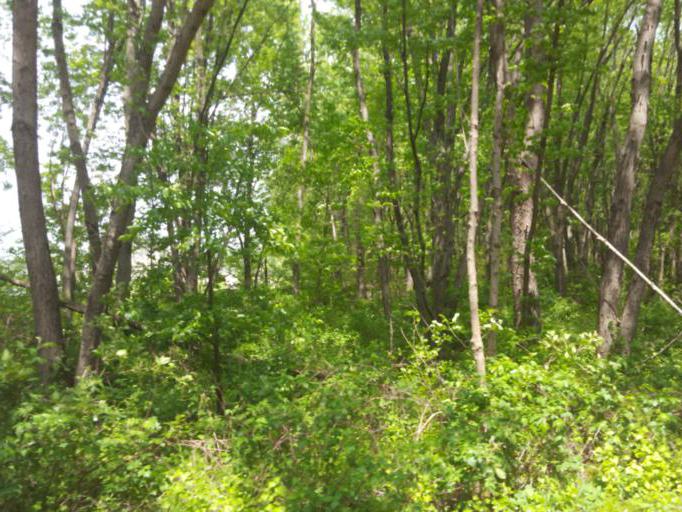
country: US
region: Ohio
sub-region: Fairfield County
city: Fairfield Beach
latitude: 39.9207
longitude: -82.4686
